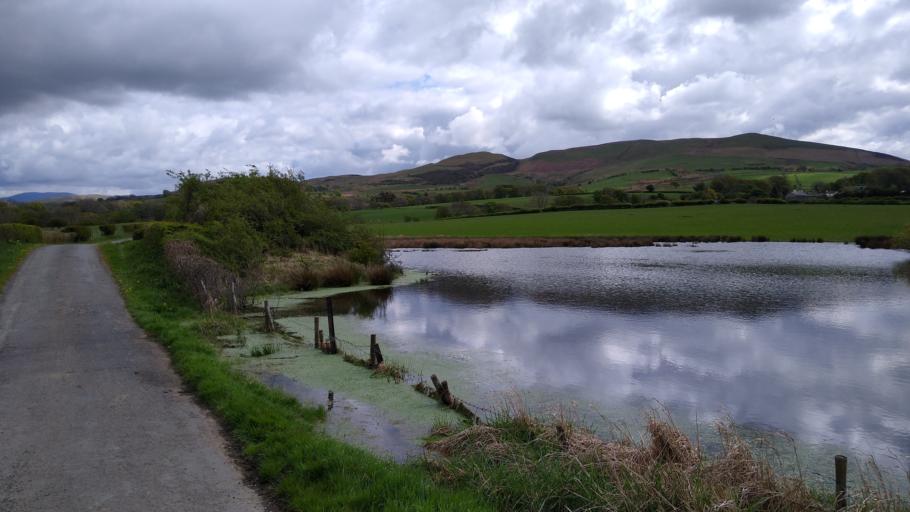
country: GB
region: England
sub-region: Cumbria
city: Cockermouth
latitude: 54.6170
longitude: -3.3777
